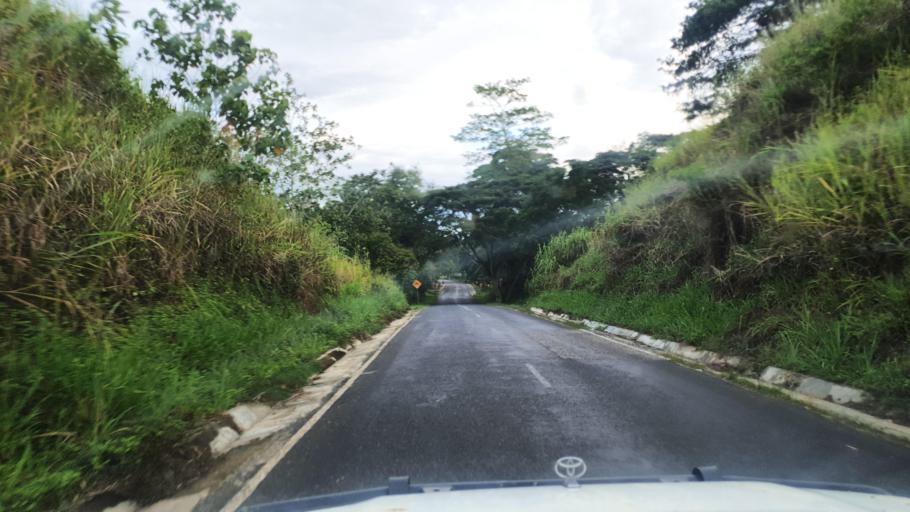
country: PG
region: National Capital
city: Port Moresby
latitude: -9.0342
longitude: 147.0438
